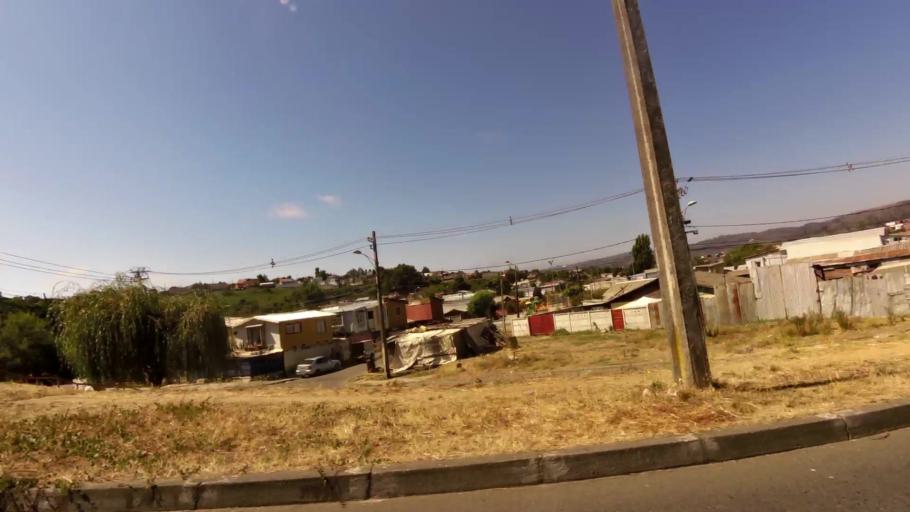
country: CL
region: Biobio
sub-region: Provincia de Concepcion
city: Concepcion
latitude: -36.7922
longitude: -73.0407
